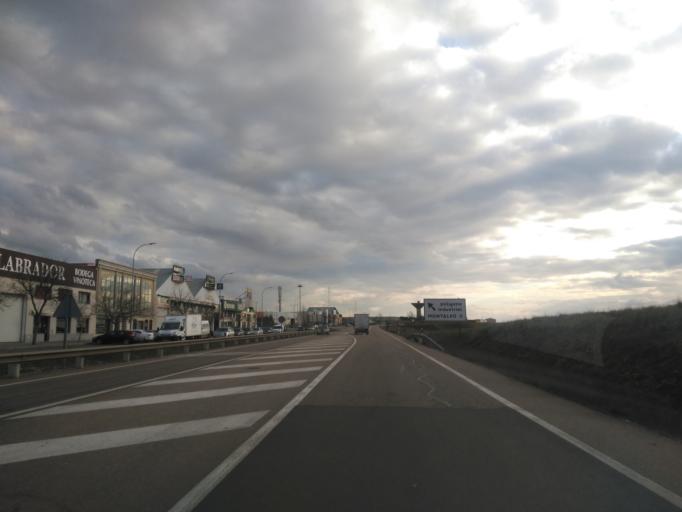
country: ES
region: Castille and Leon
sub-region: Provincia de Salamanca
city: Carbajosa de la Sagrada
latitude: 40.9390
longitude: -5.6686
